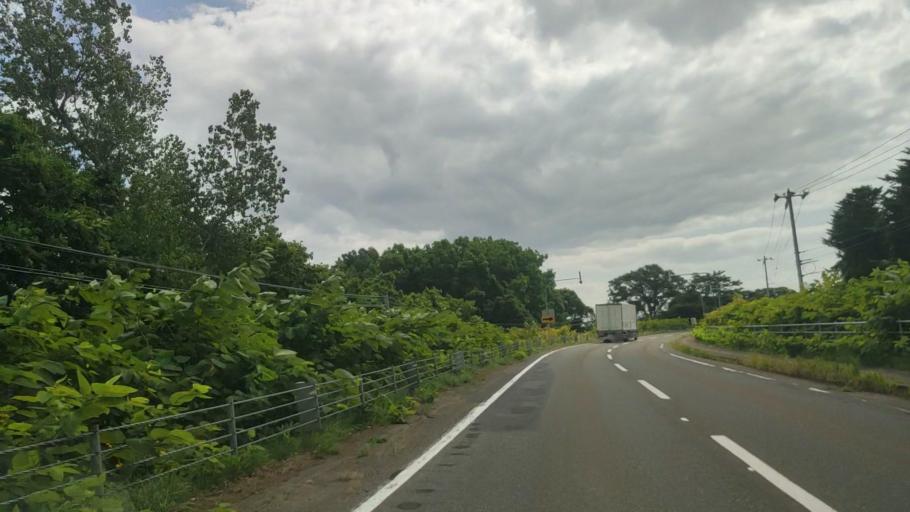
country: JP
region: Hokkaido
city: Rumoi
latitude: 44.5603
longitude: 141.7858
